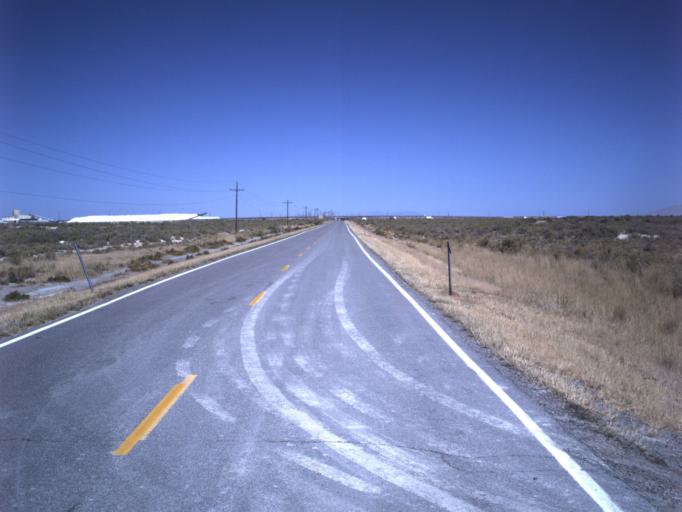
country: US
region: Utah
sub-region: Tooele County
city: Grantsville
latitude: 40.7332
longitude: -112.6567
